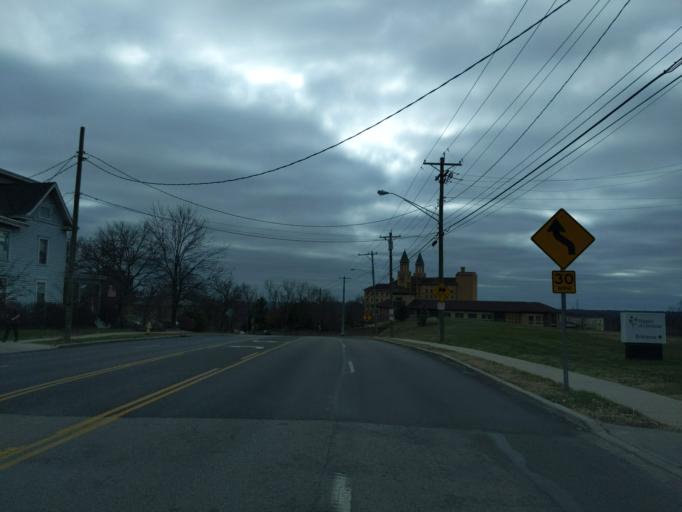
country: US
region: Ohio
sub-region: Hamilton County
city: Finneytown
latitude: 39.1900
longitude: -84.5463
